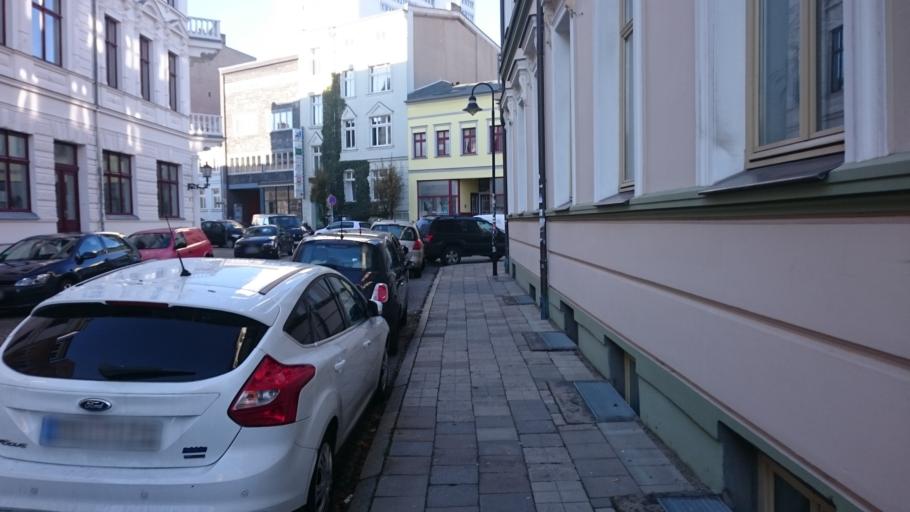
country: DE
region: Mecklenburg-Vorpommern
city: Rostock
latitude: 54.0836
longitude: 12.1332
